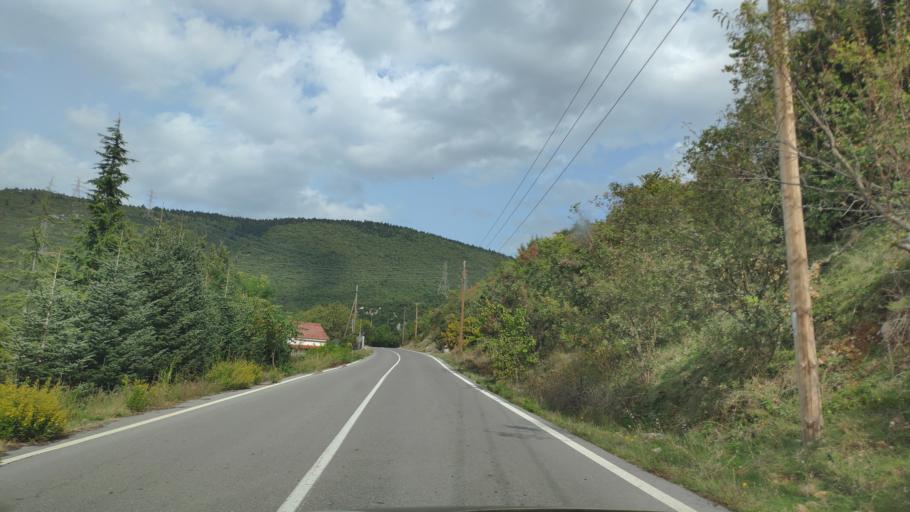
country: GR
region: Central Greece
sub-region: Nomos Fthiotidos
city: Anthili
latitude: 38.7458
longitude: 22.4515
